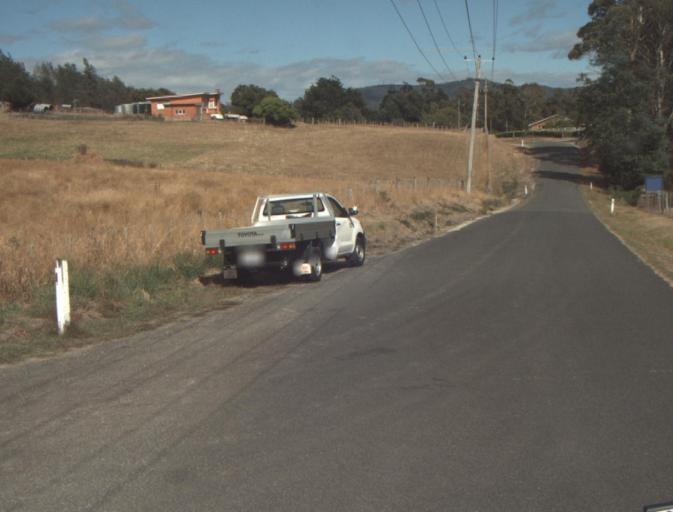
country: AU
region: Tasmania
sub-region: Launceston
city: Mayfield
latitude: -41.2583
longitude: 147.1919
